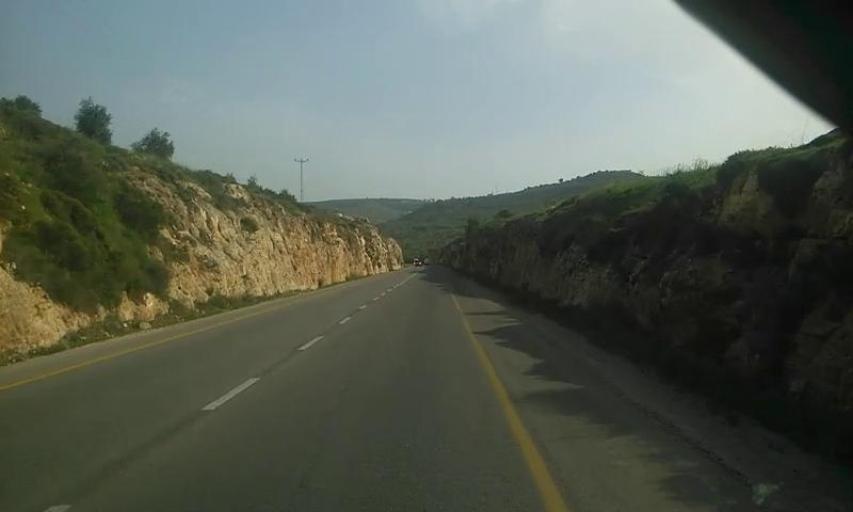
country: PS
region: West Bank
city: Jit
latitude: 32.2281
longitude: 35.1721
